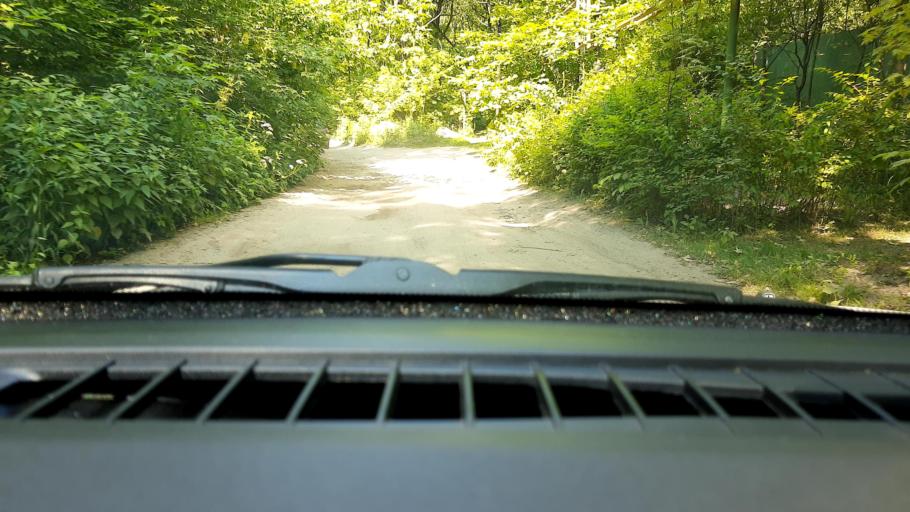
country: RU
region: Nizjnij Novgorod
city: Burevestnik
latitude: 56.1943
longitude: 43.7784
